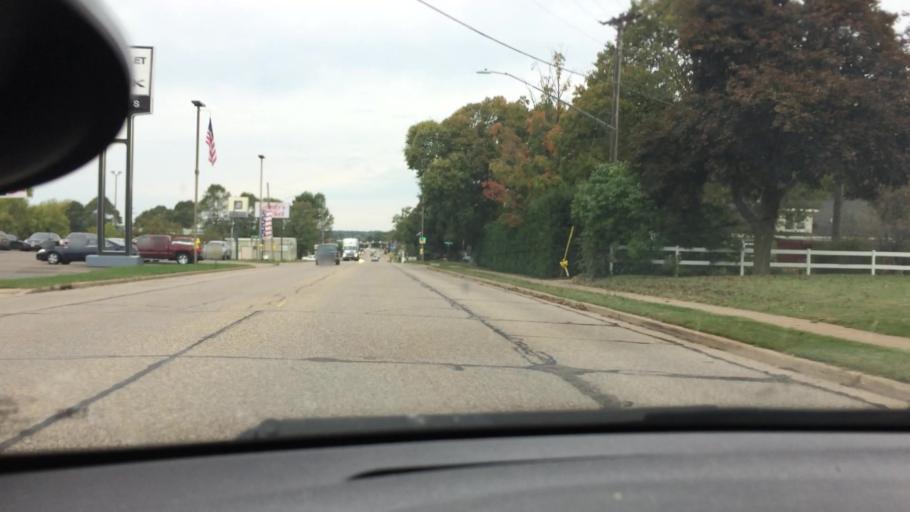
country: US
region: Wisconsin
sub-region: Clark County
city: Neillsville
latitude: 44.5527
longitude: -90.5908
